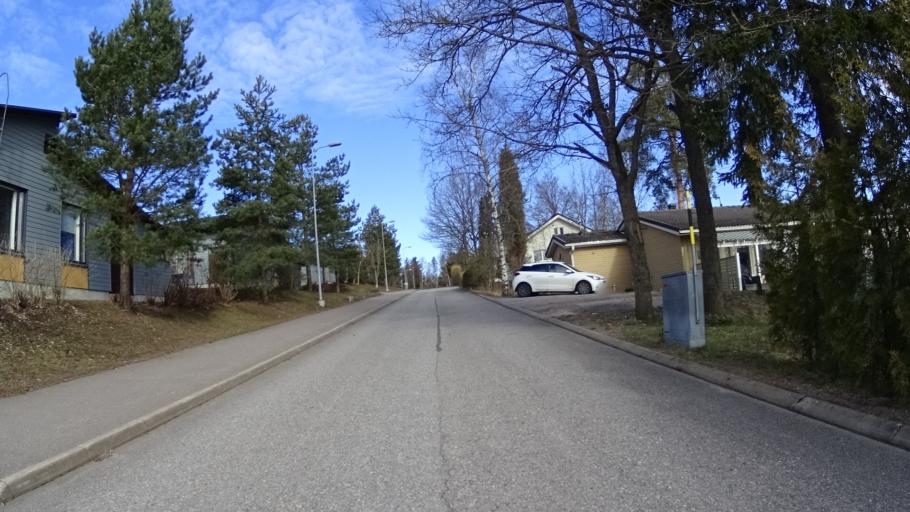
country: FI
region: Uusimaa
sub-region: Helsinki
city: Kauniainen
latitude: 60.2431
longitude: 24.7216
